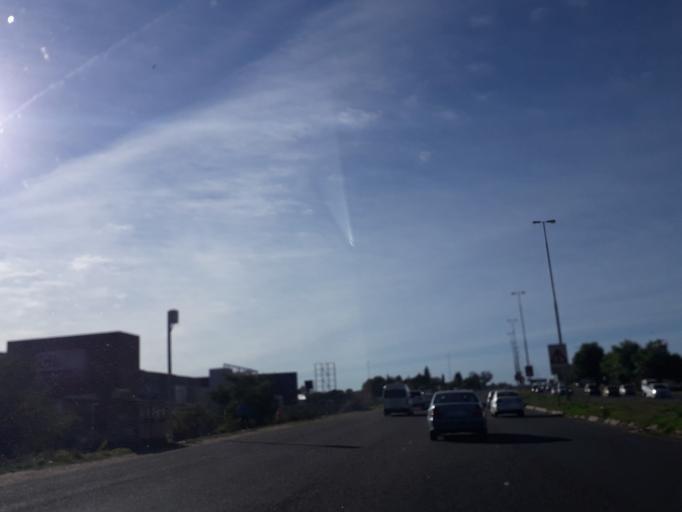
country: ZA
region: Gauteng
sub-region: City of Johannesburg Metropolitan Municipality
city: Roodepoort
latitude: -26.1308
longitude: 27.9124
